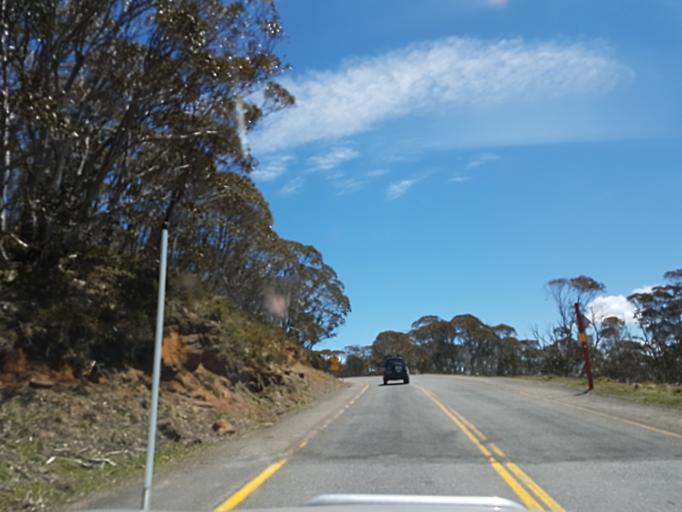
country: AU
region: Victoria
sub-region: Alpine
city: Mount Beauty
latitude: -37.0206
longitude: 147.2623
